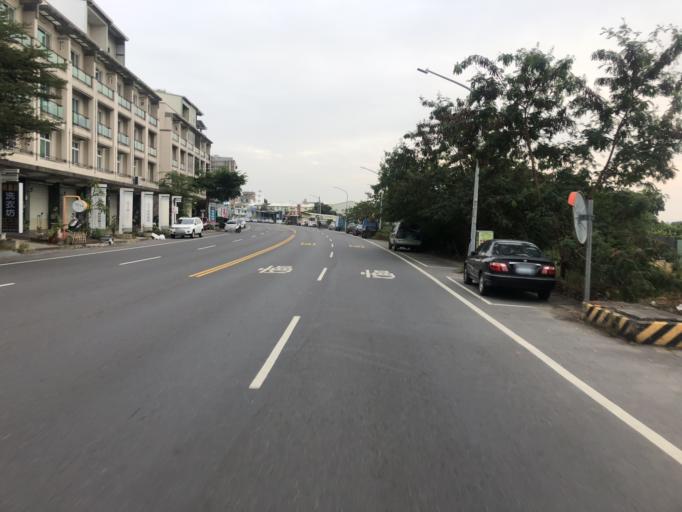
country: TW
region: Taiwan
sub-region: Tainan
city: Tainan
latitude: 23.1306
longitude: 120.2850
